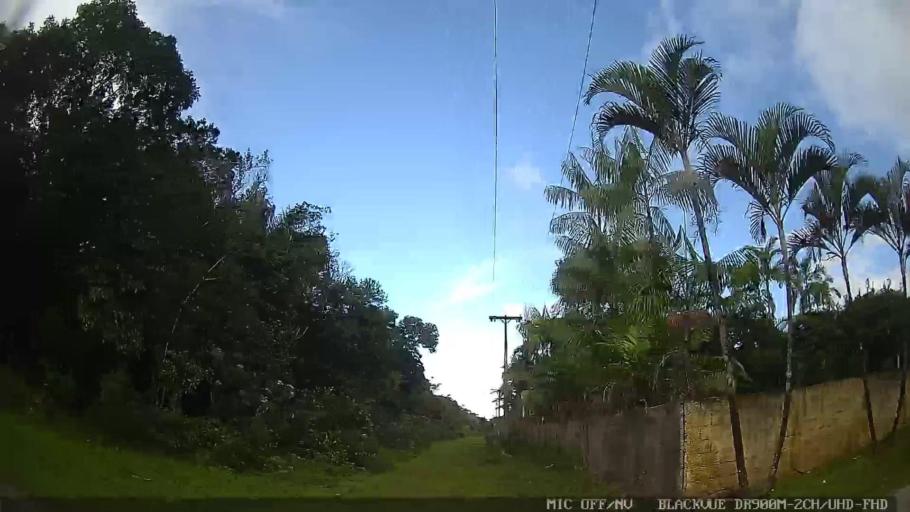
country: BR
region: Sao Paulo
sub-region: Itanhaem
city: Itanhaem
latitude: -24.1738
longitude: -46.9317
